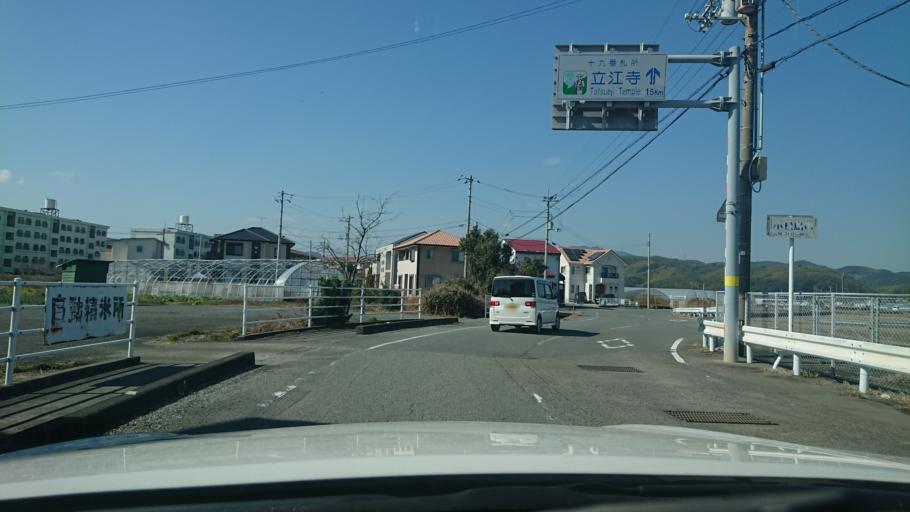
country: JP
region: Tokushima
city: Komatsushimacho
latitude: 33.9639
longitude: 134.6173
